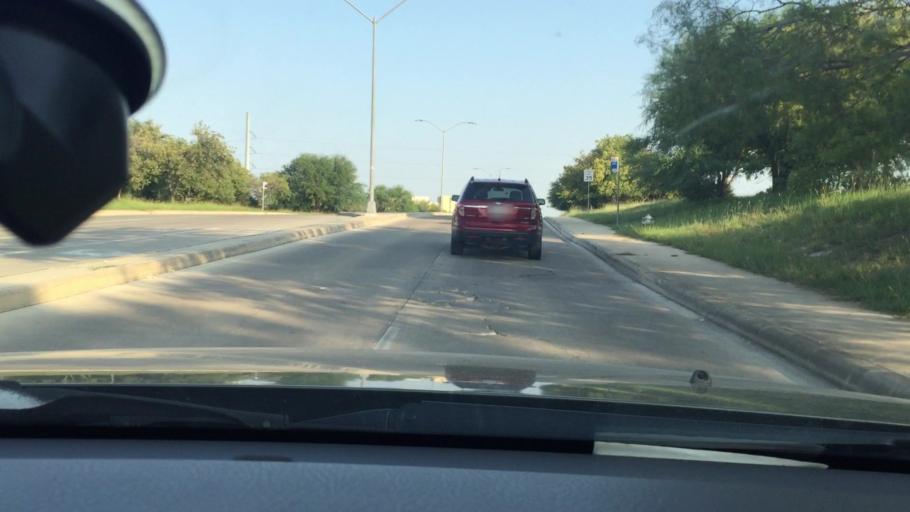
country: US
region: Texas
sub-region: Bexar County
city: Leon Valley
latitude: 29.5198
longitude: -98.5881
